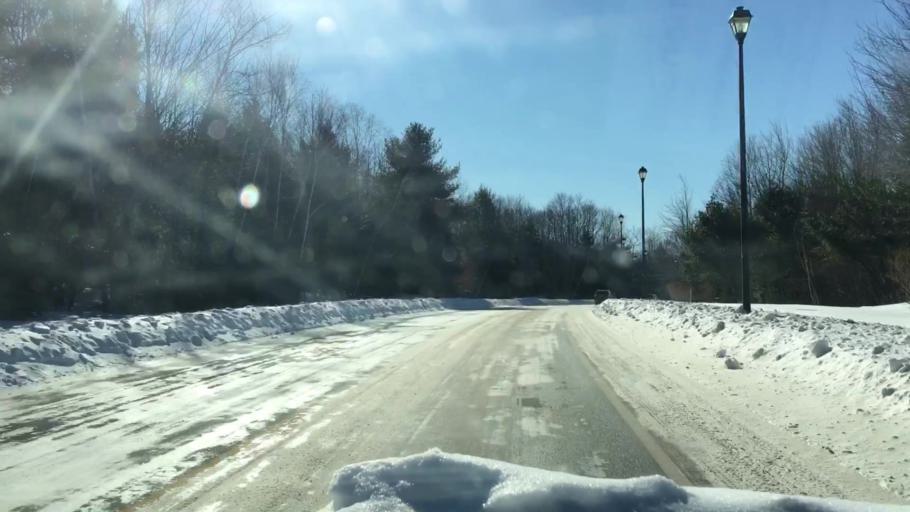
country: US
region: Maine
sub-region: Sagadahoc County
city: Topsham
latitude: 43.9434
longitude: -69.9534
